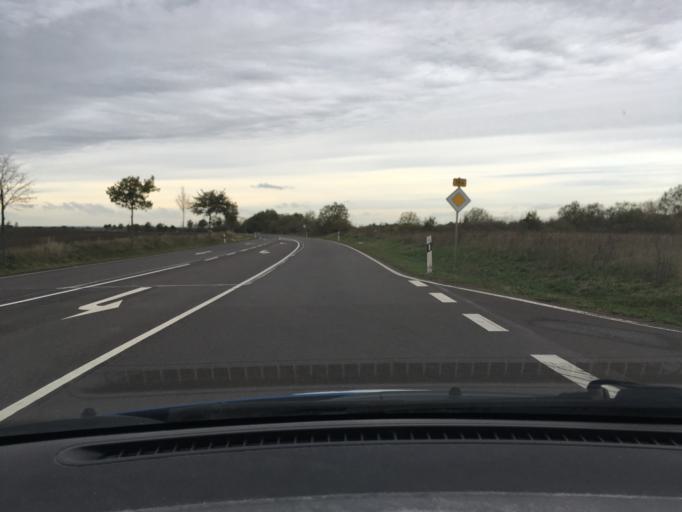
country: DE
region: Saxony-Anhalt
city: Leitzkau
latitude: 52.0478
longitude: 11.9672
